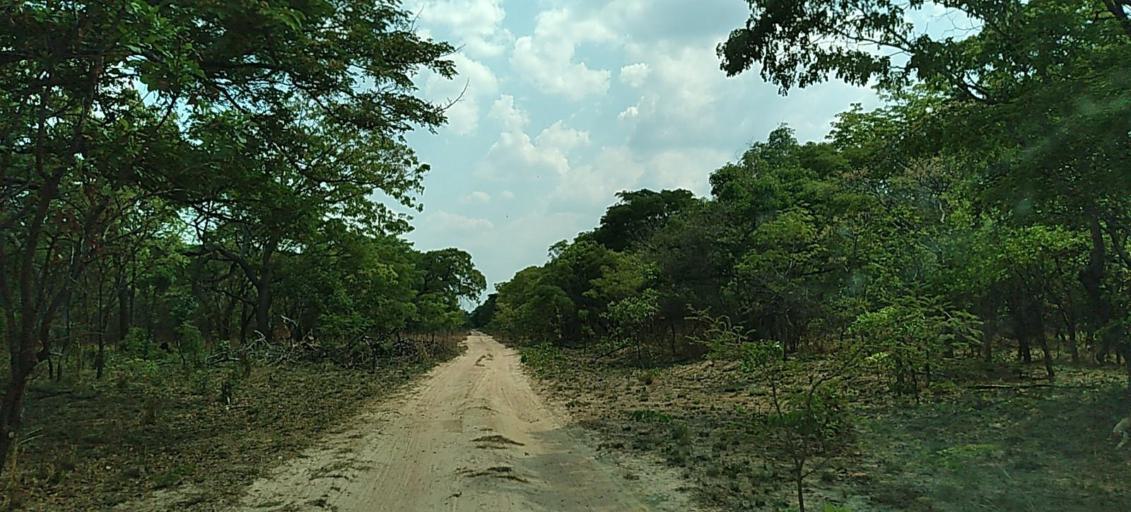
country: ZM
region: Copperbelt
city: Mpongwe
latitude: -13.8528
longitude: 27.9307
